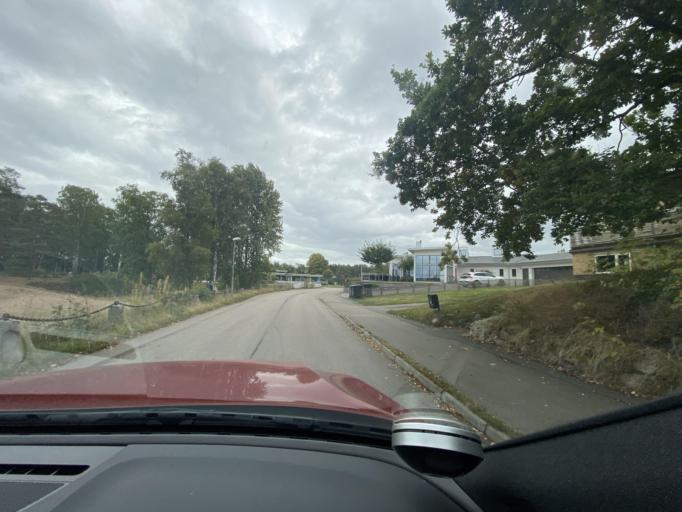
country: SE
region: Kronoberg
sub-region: Markaryds Kommun
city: Markaryd
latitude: 56.4619
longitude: 13.6032
